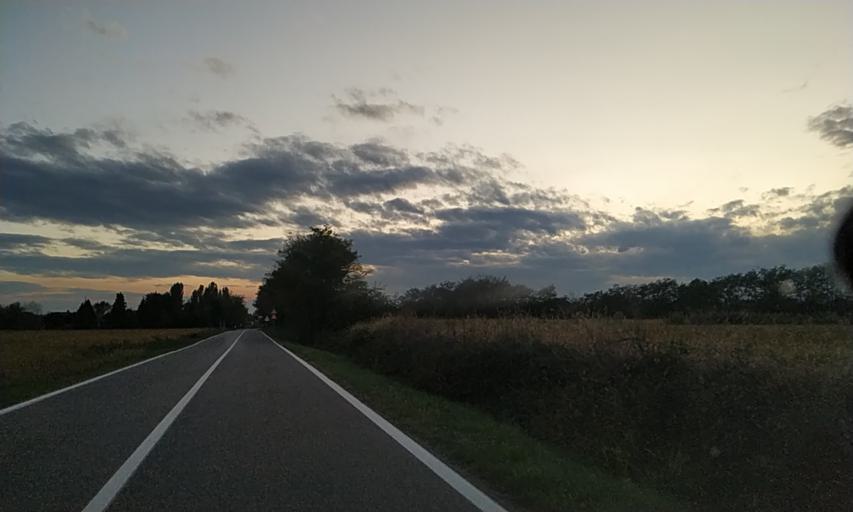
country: IT
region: Piedmont
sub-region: Provincia di Vercelli
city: Buronzo
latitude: 45.4867
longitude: 8.2785
